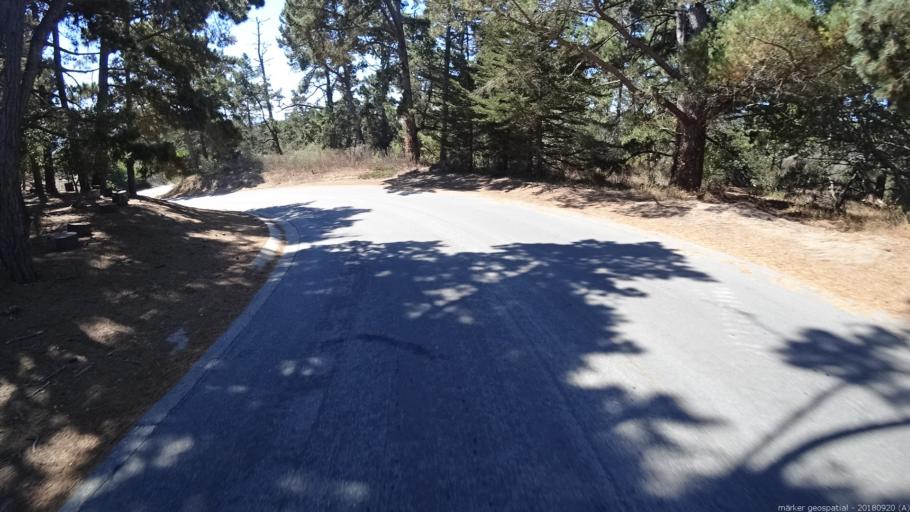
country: US
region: California
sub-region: Monterey County
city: Carmel-by-the-Sea
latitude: 36.5690
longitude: -121.9111
